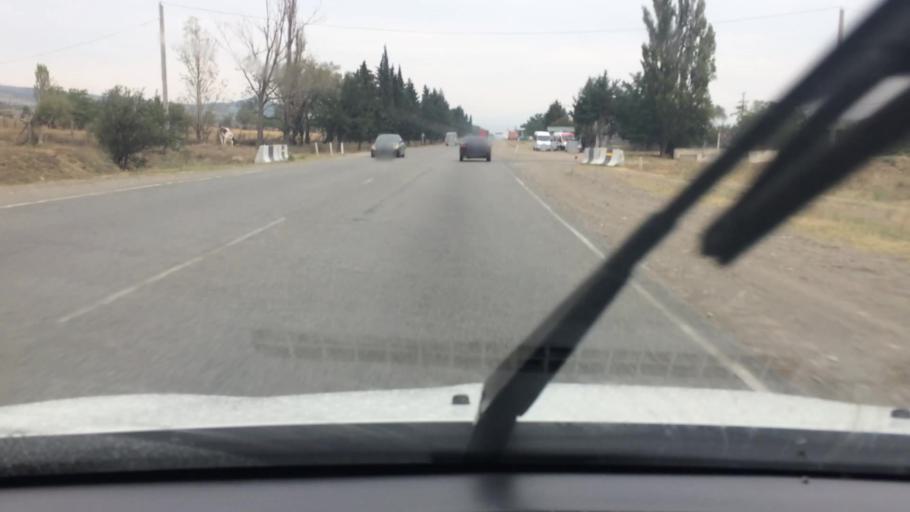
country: GE
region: T'bilisi
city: Tbilisi
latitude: 41.6308
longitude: 44.8113
